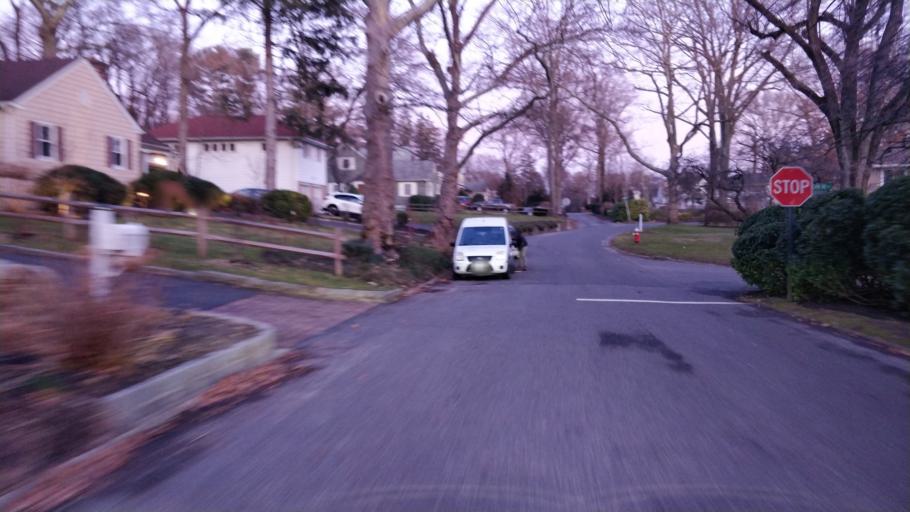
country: US
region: New York
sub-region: Nassau County
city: Glen Cove
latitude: 40.8682
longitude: -73.6500
